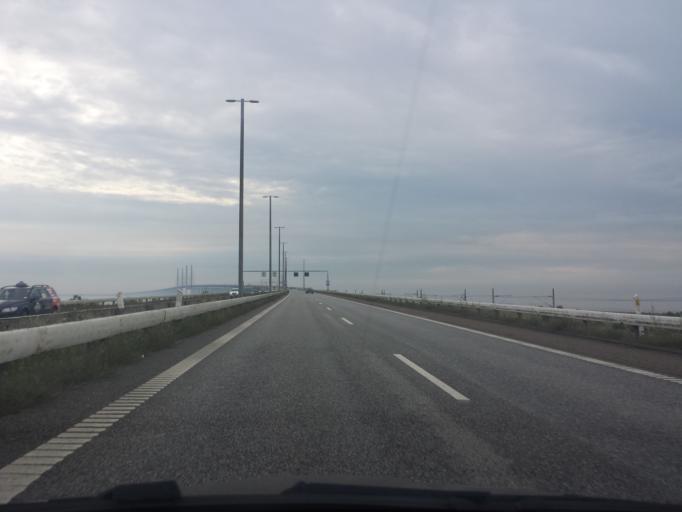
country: DK
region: Capital Region
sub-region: Dragor Kommune
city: Dragor
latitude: 55.5941
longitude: 12.7643
